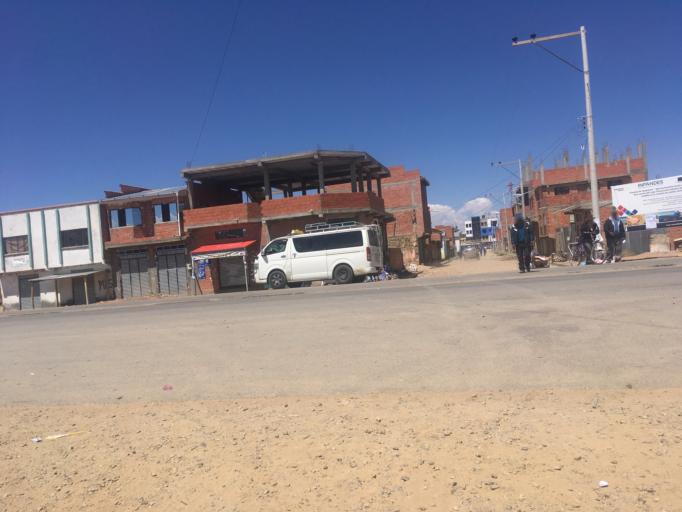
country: BO
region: La Paz
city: Huatajata
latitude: -16.1901
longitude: -68.7443
